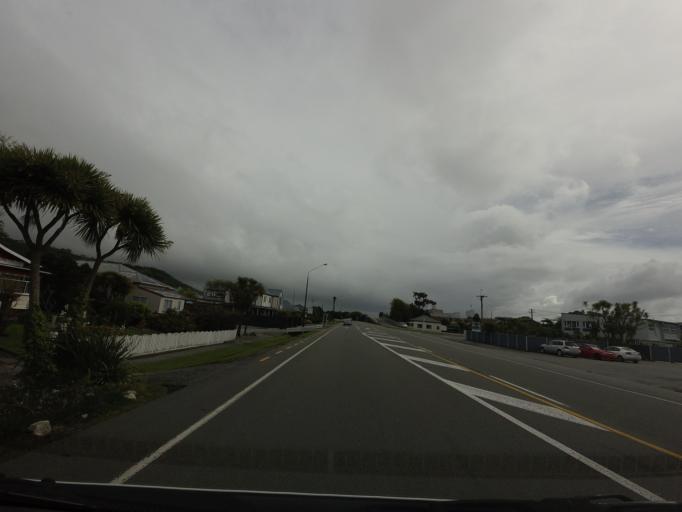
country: NZ
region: West Coast
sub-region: Grey District
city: Greymouth
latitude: -42.4630
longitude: 171.1955
